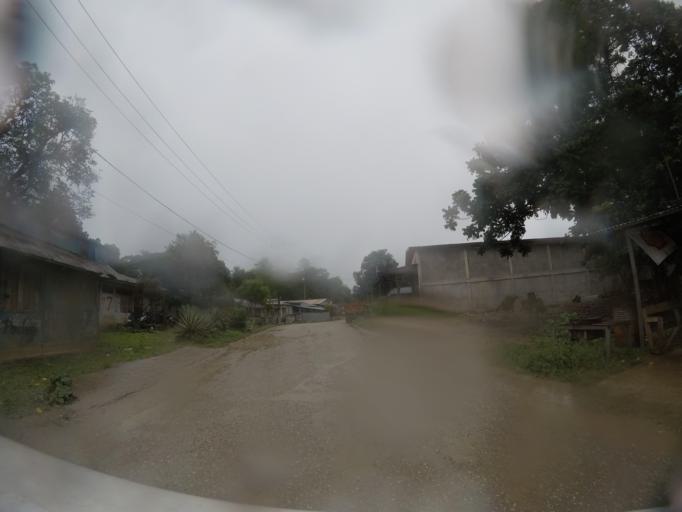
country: TL
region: Lautem
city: Lospalos
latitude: -8.5198
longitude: 126.9990
